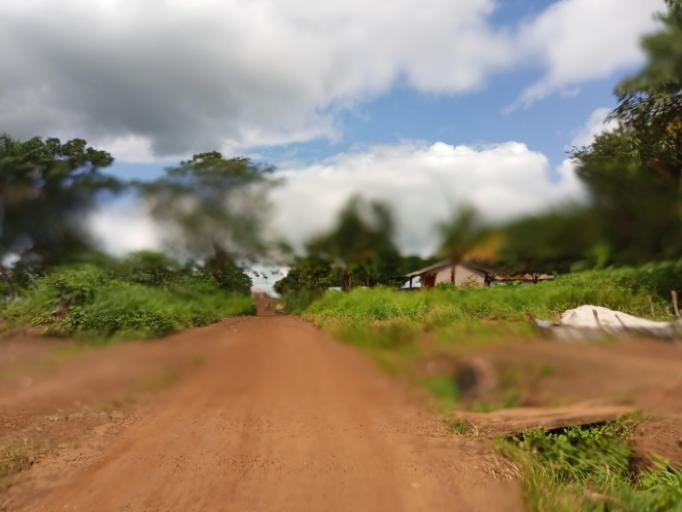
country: SL
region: Northern Province
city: Kamakwie
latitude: 9.5041
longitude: -12.2341
